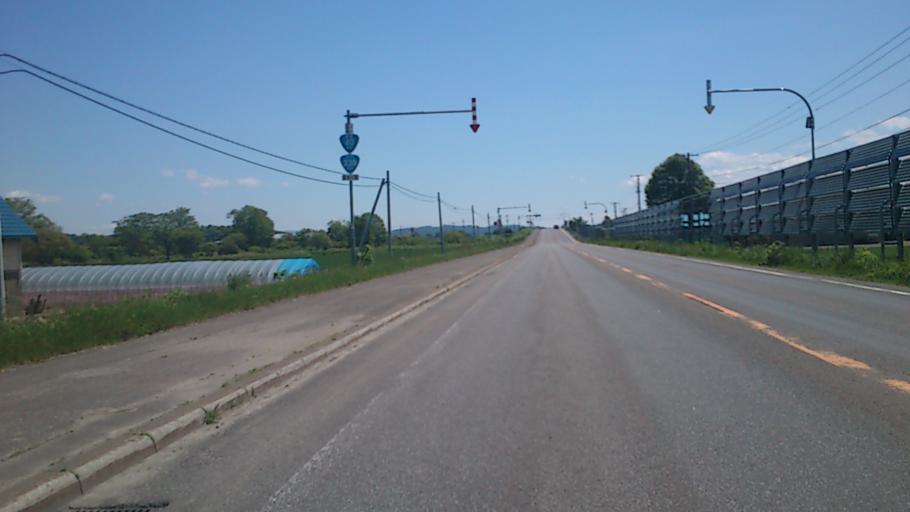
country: JP
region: Hokkaido
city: Nayoro
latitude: 44.2003
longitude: 142.3951
